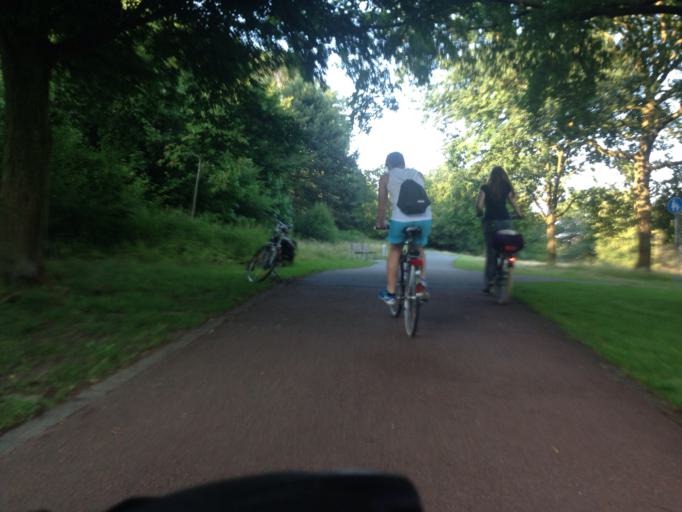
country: DE
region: North Rhine-Westphalia
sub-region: Regierungsbezirk Munster
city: Muenster
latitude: 51.9490
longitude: 7.5989
